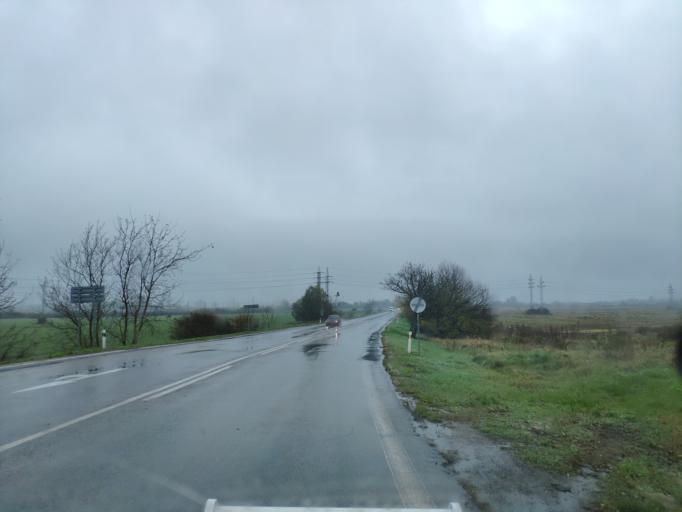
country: SK
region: Kosicky
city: Cierna nad Tisou
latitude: 48.4298
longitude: 21.9849
